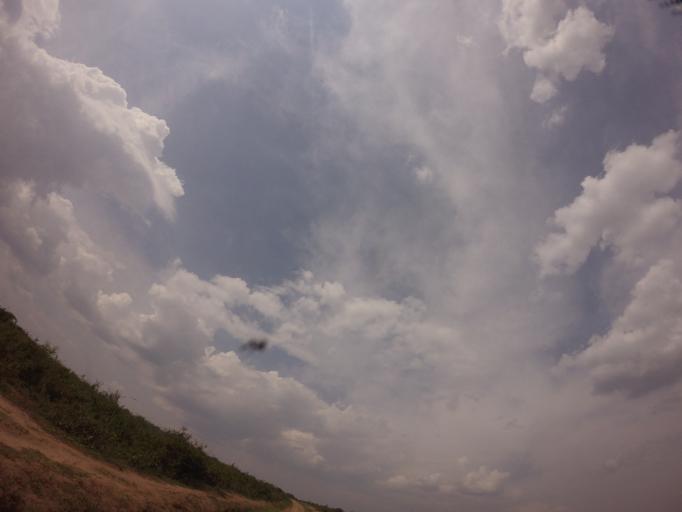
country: UG
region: Western Region
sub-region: Rubirizi District
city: Rubirizi
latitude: -0.2092
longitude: 29.9013
